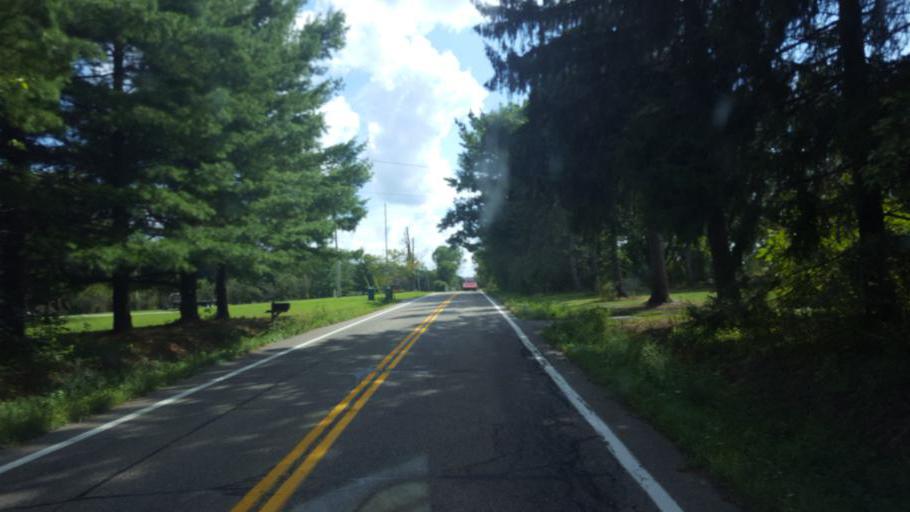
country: US
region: Ohio
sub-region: Portage County
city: Hiram
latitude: 41.2705
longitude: -81.1454
